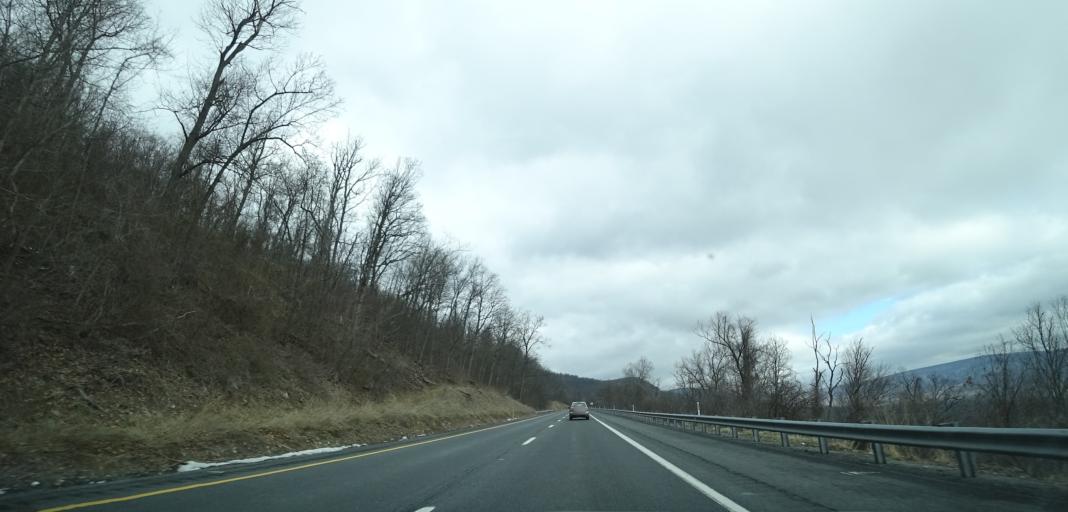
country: US
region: Pennsylvania
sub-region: Bedford County
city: Earlston
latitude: 39.8580
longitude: -78.2668
